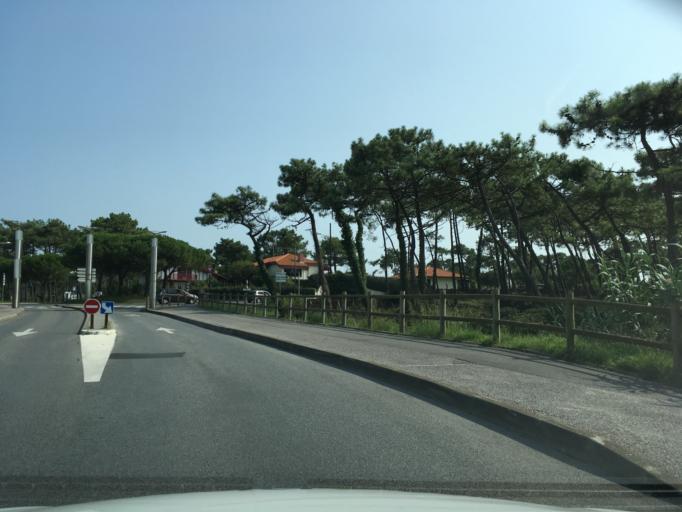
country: FR
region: Aquitaine
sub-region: Departement des Pyrenees-Atlantiques
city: Anglet
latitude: 43.5263
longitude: -1.5178
